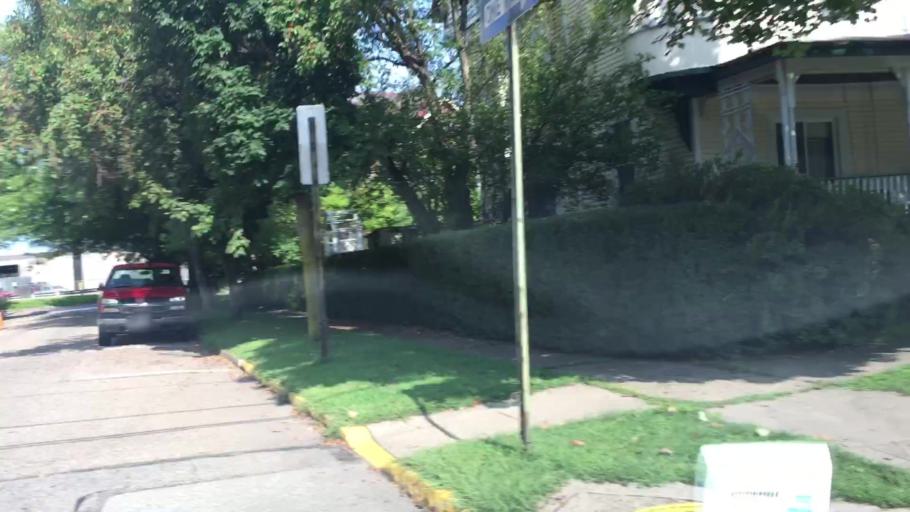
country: US
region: Pennsylvania
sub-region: Allegheny County
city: Aspinwall
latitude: 40.4922
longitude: -79.9069
